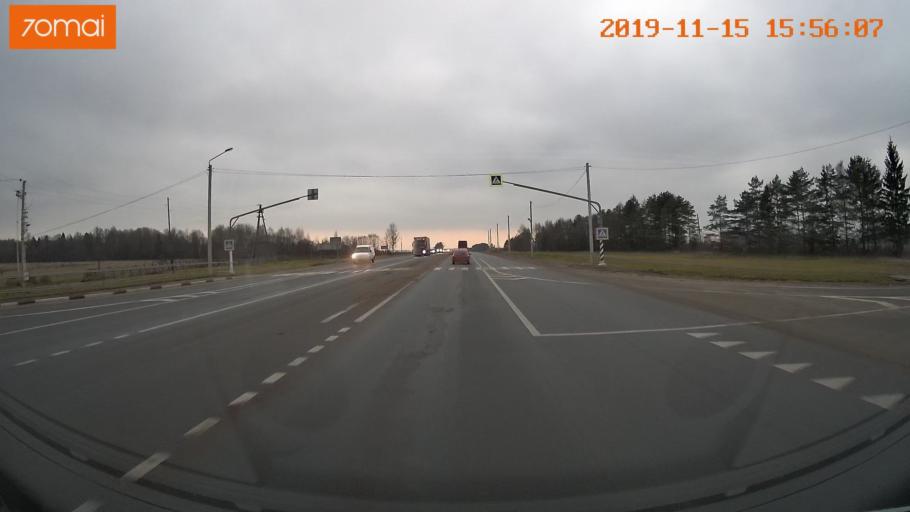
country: RU
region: Jaroslavl
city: Yaroslavl
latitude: 57.8456
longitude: 39.9767
